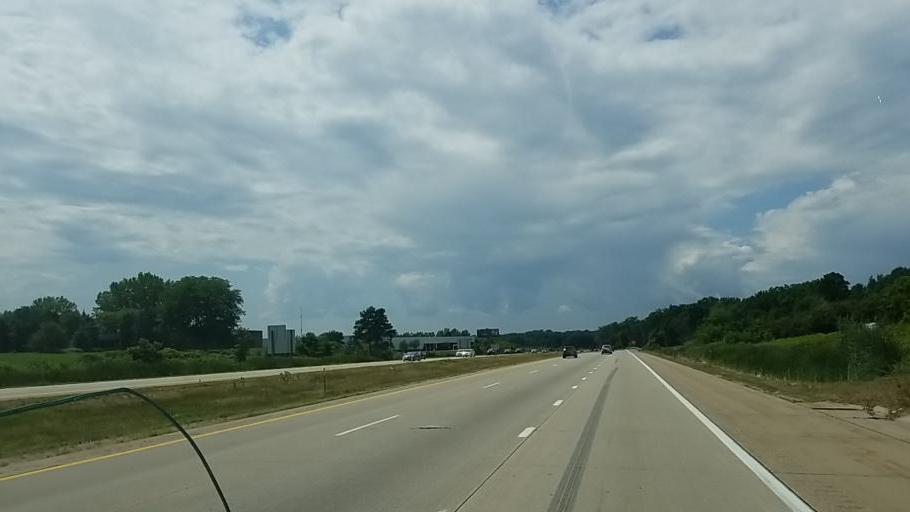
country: US
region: Michigan
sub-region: Kent County
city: Comstock Park
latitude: 43.0212
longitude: -85.7136
